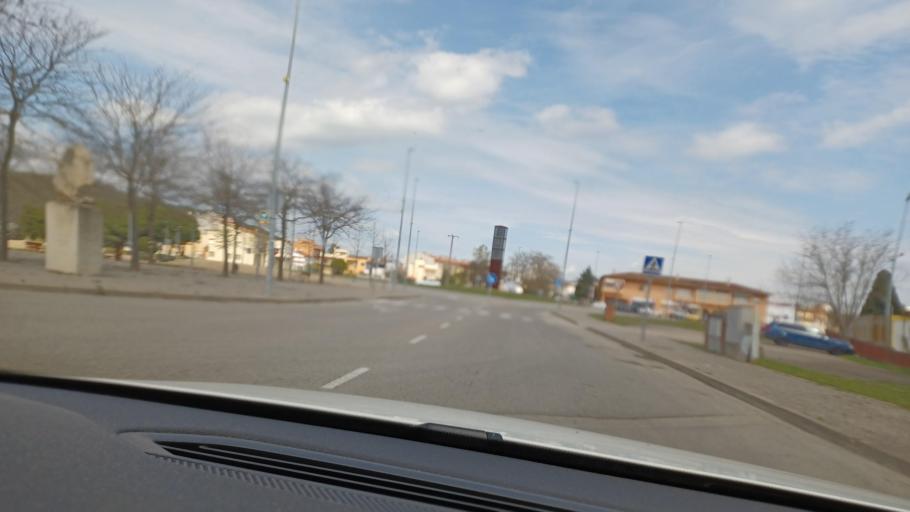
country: ES
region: Catalonia
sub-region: Provincia de Girona
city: Sarria de Ter
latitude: 42.0146
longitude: 2.8219
